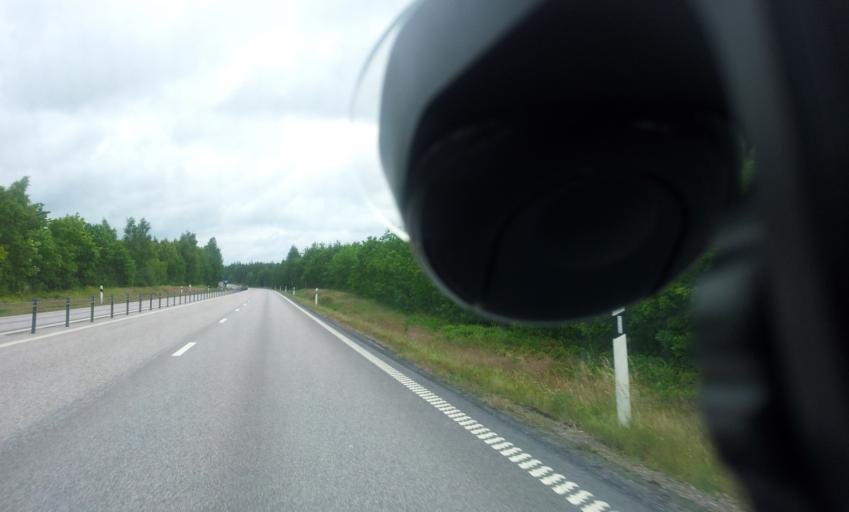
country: SE
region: Kalmar
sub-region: Monsteras Kommun
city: Timmernabben
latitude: 56.9879
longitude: 16.4083
